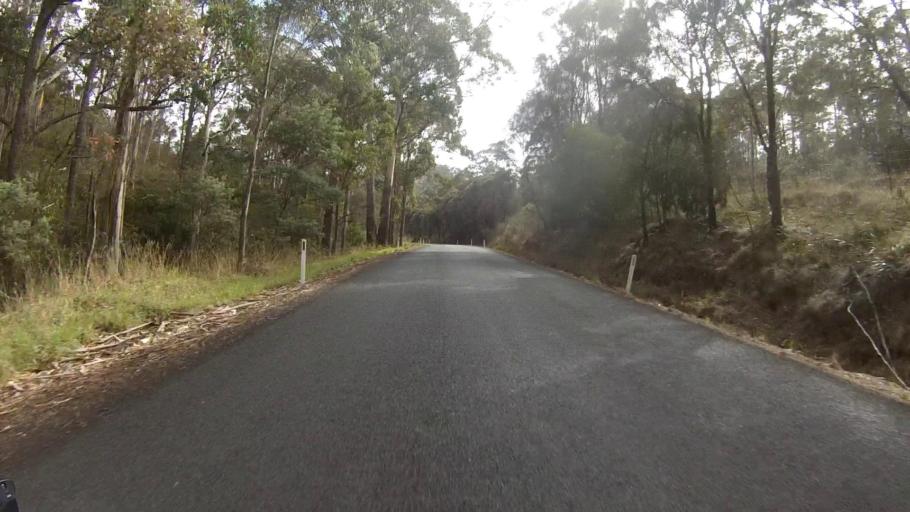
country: AU
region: Tasmania
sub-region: Sorell
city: Sorell
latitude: -42.8120
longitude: 147.7929
